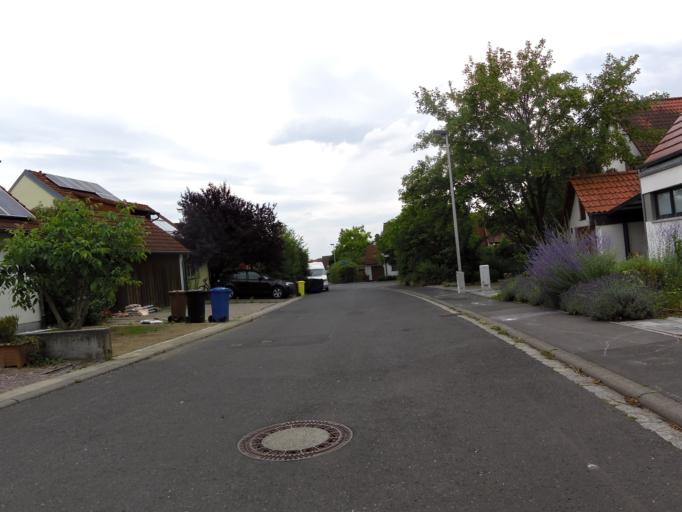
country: DE
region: Bavaria
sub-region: Regierungsbezirk Unterfranken
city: Eibelstadt
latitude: 49.7235
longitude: 9.9733
